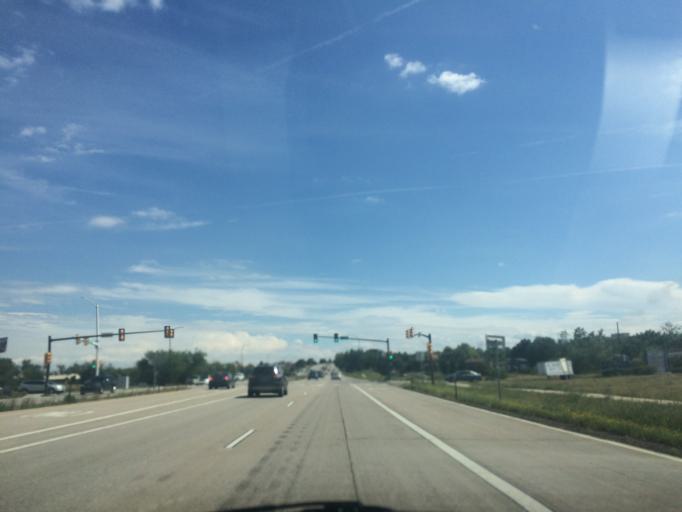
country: US
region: Colorado
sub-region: Broomfield County
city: Broomfield
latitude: 39.8682
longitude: -105.0882
